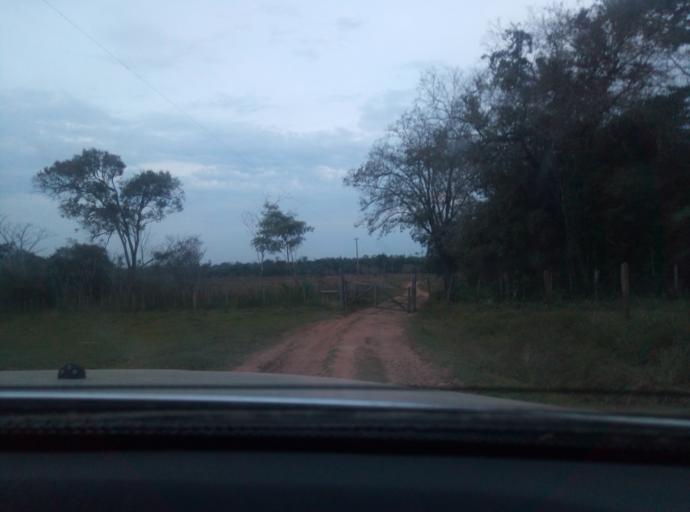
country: PY
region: Caaguazu
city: Carayao
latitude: -25.1467
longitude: -56.3821
